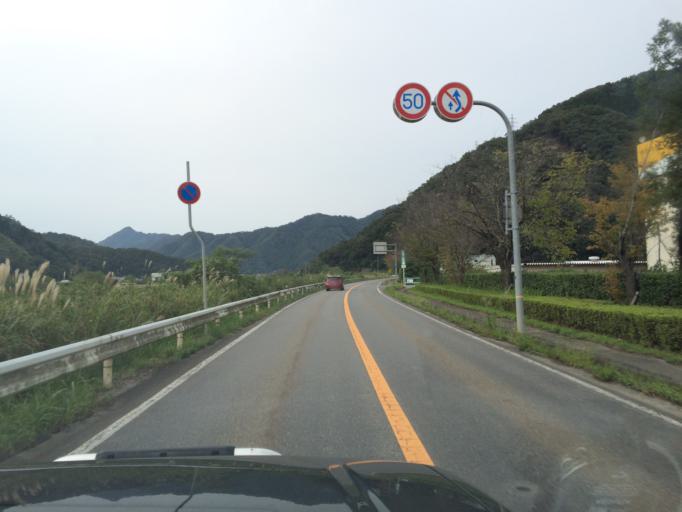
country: JP
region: Hyogo
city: Toyooka
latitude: 35.3935
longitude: 134.7937
